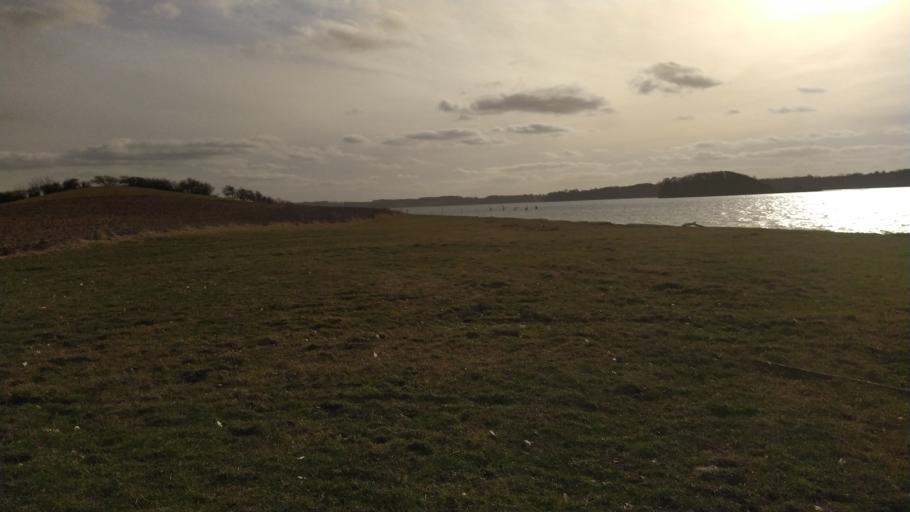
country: DK
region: South Denmark
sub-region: Fredericia Kommune
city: Taulov
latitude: 55.5154
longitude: 9.6061
